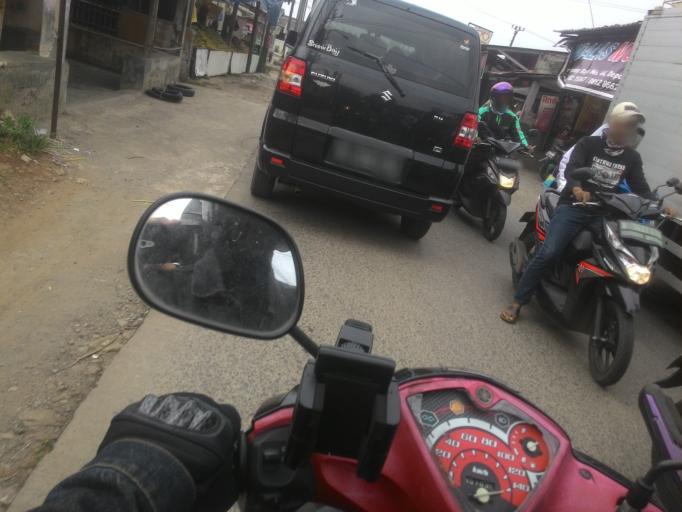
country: ID
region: West Java
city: Depok
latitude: -6.4224
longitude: 106.8378
